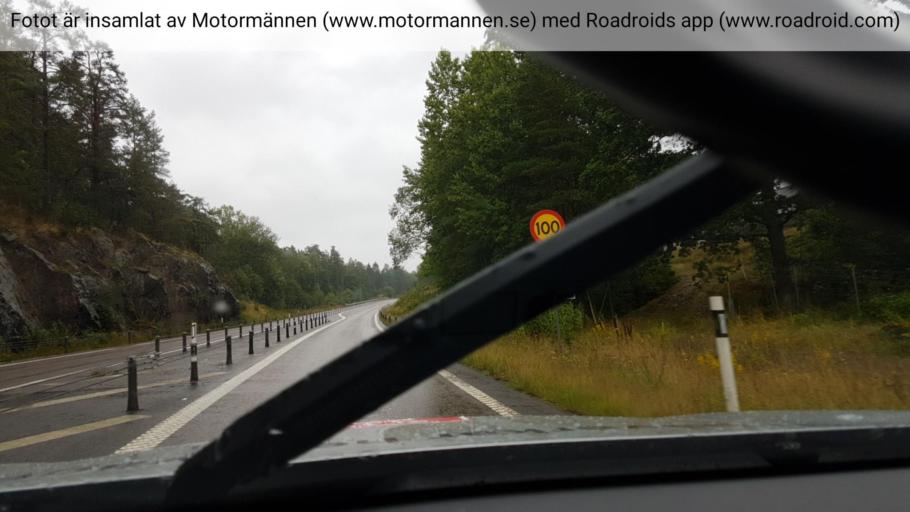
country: SE
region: Vaestra Goetaland
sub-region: Melleruds Kommun
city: Mellerud
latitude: 58.7660
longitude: 12.4903
